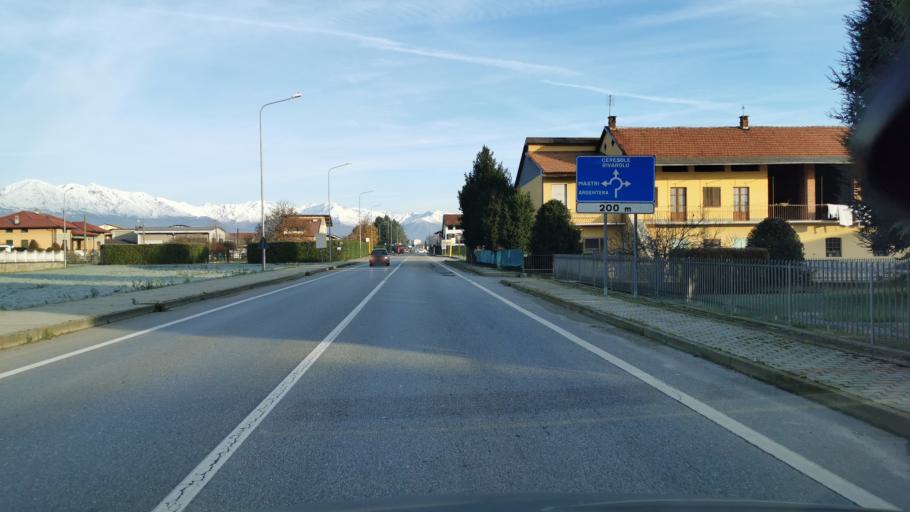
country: IT
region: Piedmont
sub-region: Provincia di Torino
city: Feletto
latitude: 45.2862
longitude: 7.7455
